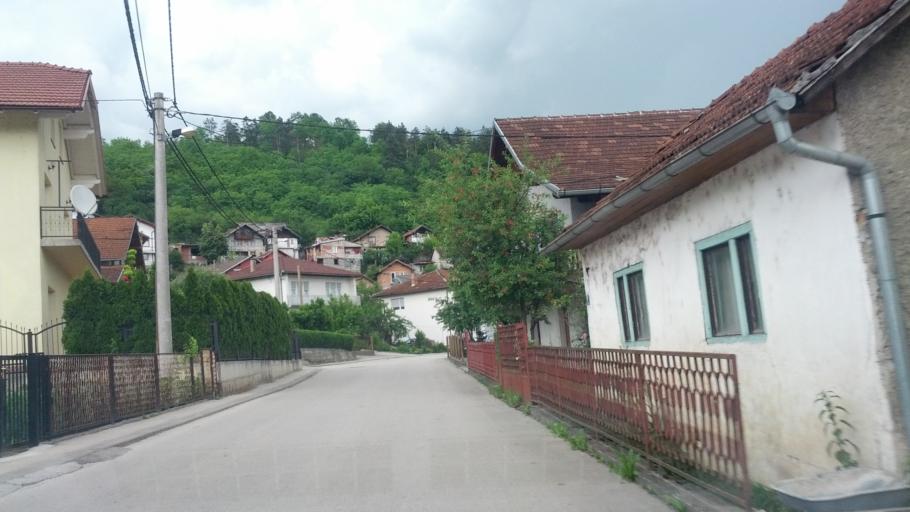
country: BA
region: Federation of Bosnia and Herzegovina
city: Bosanska Krupa
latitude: 44.8873
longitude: 16.1443
